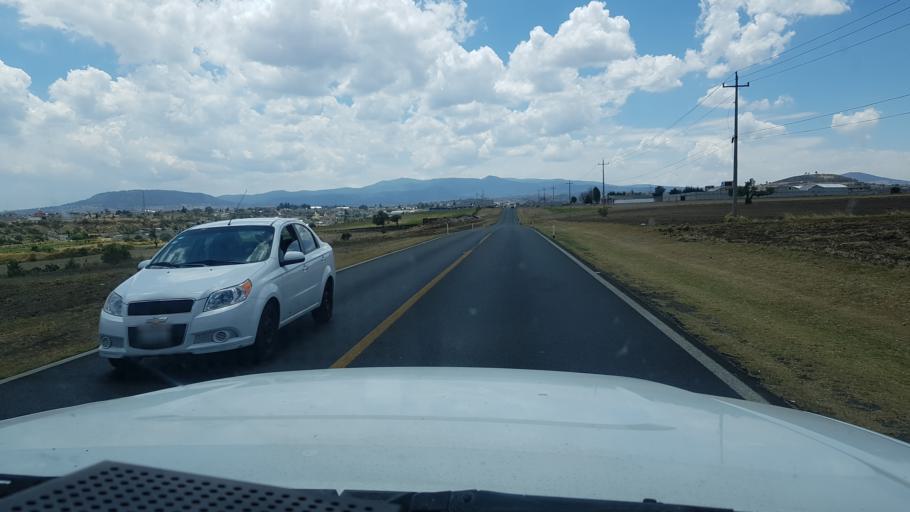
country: MX
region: Hidalgo
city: Calpulalpan
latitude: 19.6053
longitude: -98.5635
